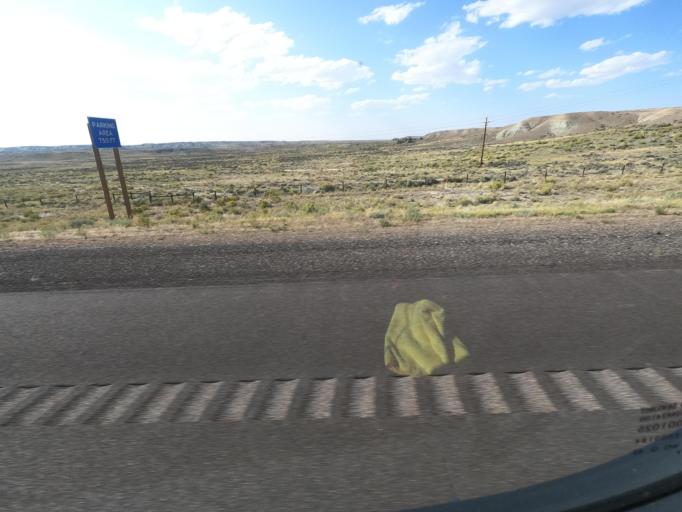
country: US
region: Wyoming
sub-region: Uinta County
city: Lyman
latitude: 41.4010
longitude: -110.1681
